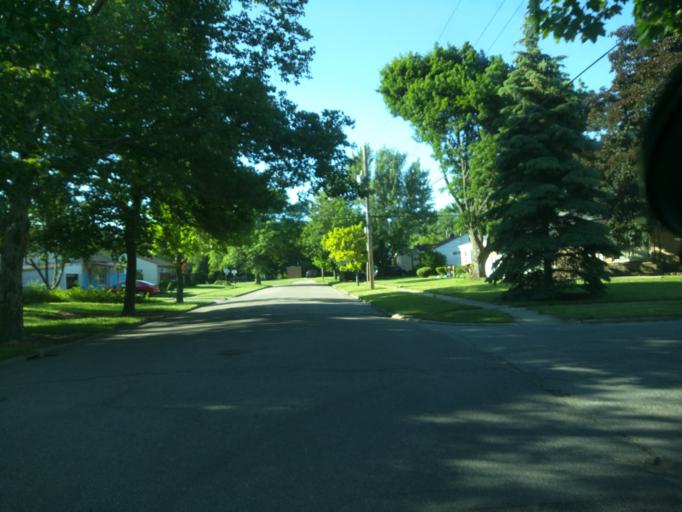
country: US
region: Michigan
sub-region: Ingham County
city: Edgemont Park
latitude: 42.7453
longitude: -84.5934
